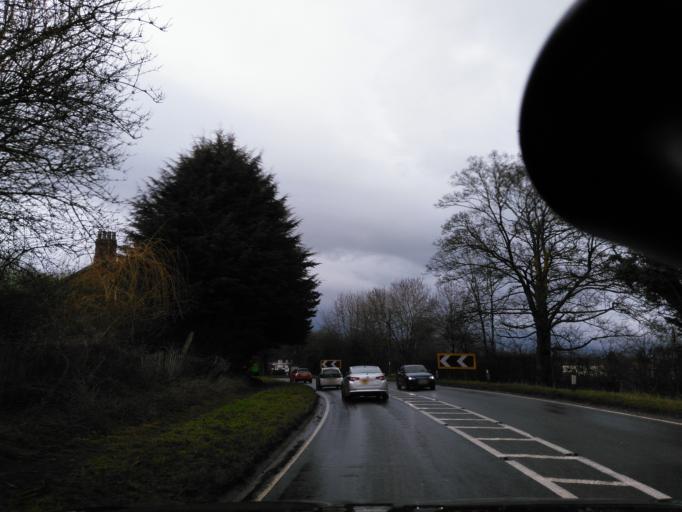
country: GB
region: England
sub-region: North Yorkshire
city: Harrogate
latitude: 54.0631
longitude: -1.5377
